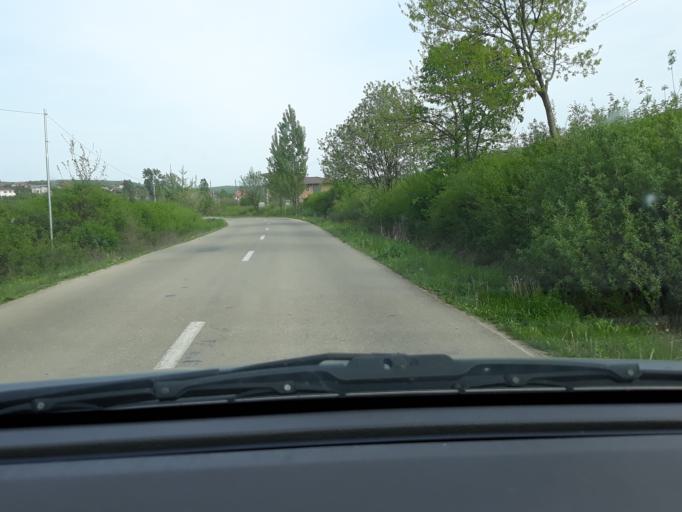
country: RO
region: Bihor
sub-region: Comuna Sanmartin
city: Sanmartin
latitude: 46.9778
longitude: 22.0030
